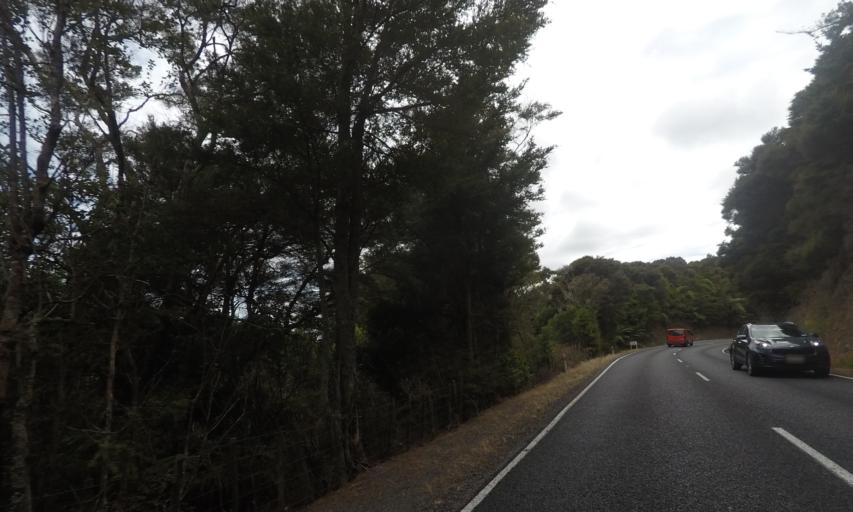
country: NZ
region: Northland
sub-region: Whangarei
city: Whangarei
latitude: -35.7647
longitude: 174.4639
